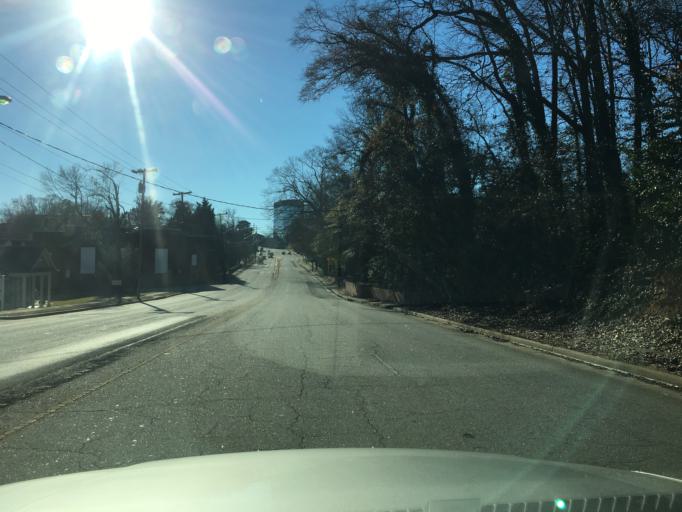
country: US
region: South Carolina
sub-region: Greenville County
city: Greenville
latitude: 34.8572
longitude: -82.3883
